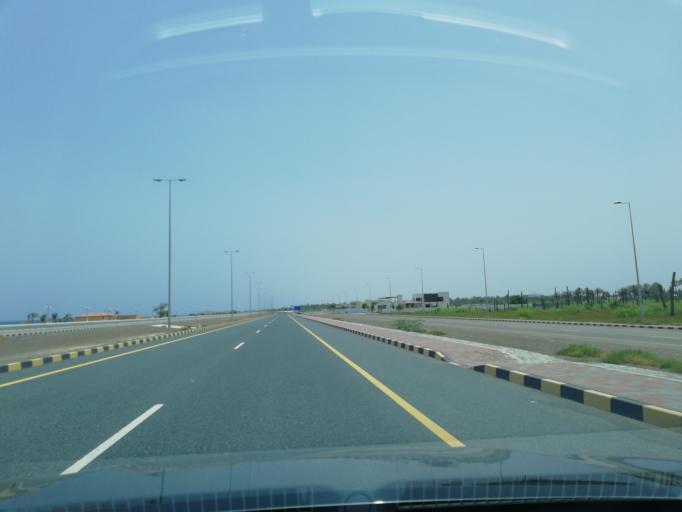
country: OM
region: Al Batinah
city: Shinas
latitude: 24.8181
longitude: 56.4414
